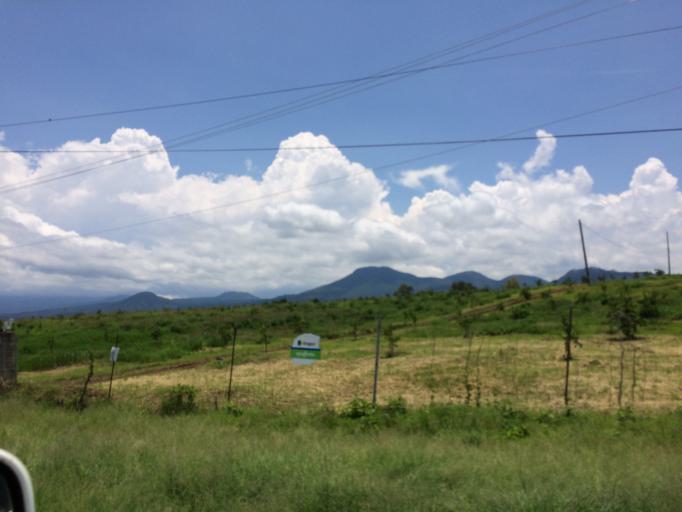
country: MX
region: Michoacan
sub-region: Periban
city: San Francisco Periban
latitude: 19.5471
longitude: -102.4072
